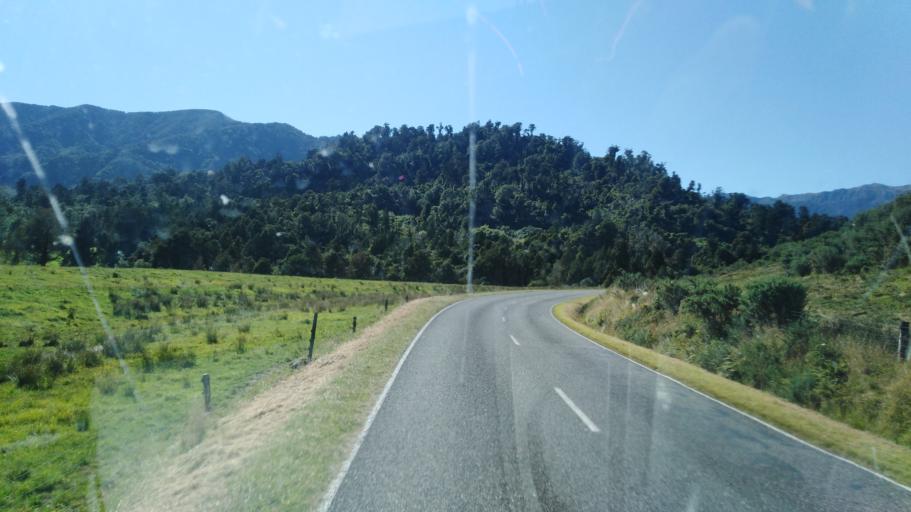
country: NZ
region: West Coast
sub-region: Buller District
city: Westport
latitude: -41.5299
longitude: 171.9876
